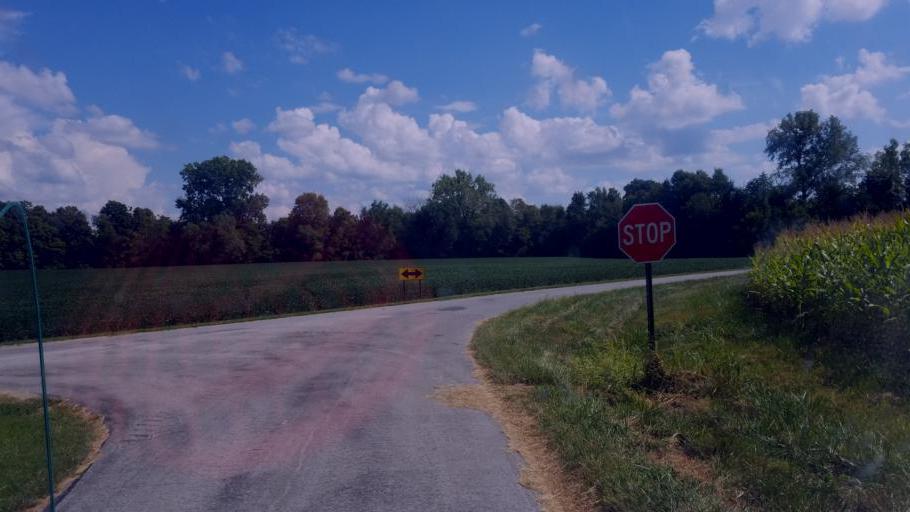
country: US
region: Ohio
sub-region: Seneca County
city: Tiffin
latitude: 40.9709
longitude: -83.1801
